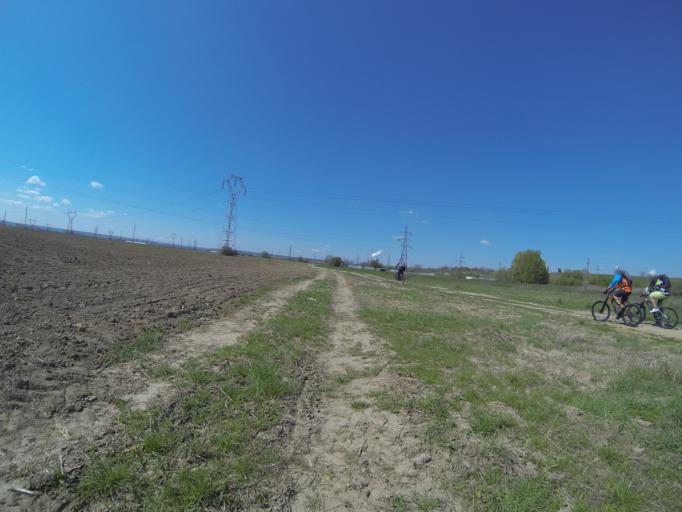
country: RO
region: Dolj
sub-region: Comuna Isalnita
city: Isalnita
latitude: 44.3899
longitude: 23.7538
